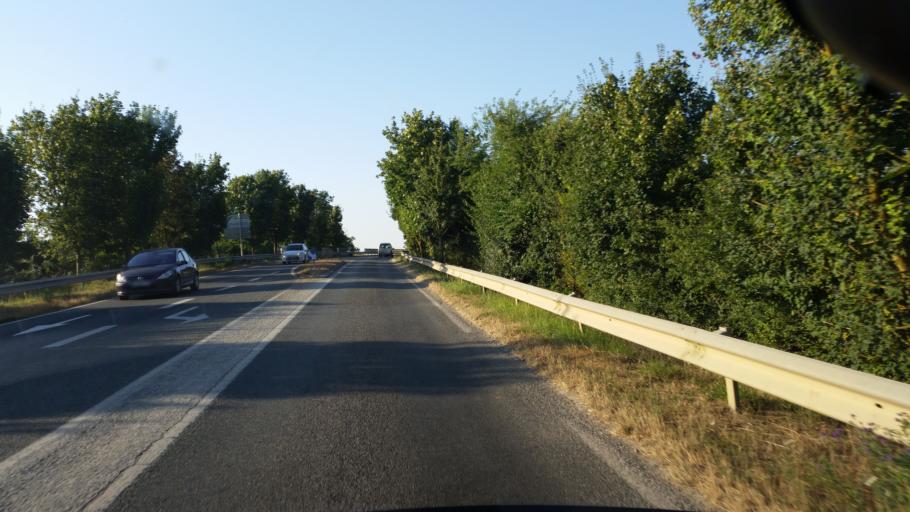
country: FR
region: Poitou-Charentes
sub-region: Departement de la Charente-Maritime
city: Saint-Jean-de-Liversay
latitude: 46.2280
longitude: -0.8789
